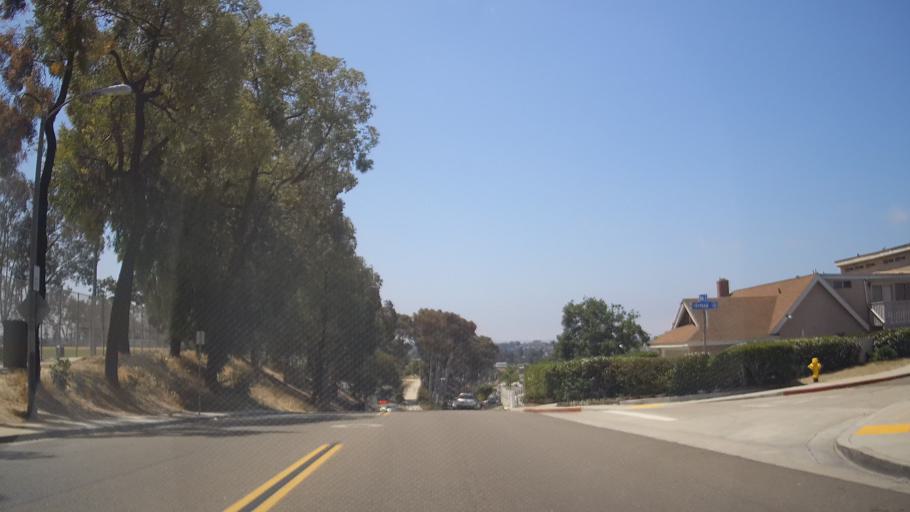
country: US
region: California
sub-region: San Diego County
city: Bonita
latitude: 32.6772
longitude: -117.0486
